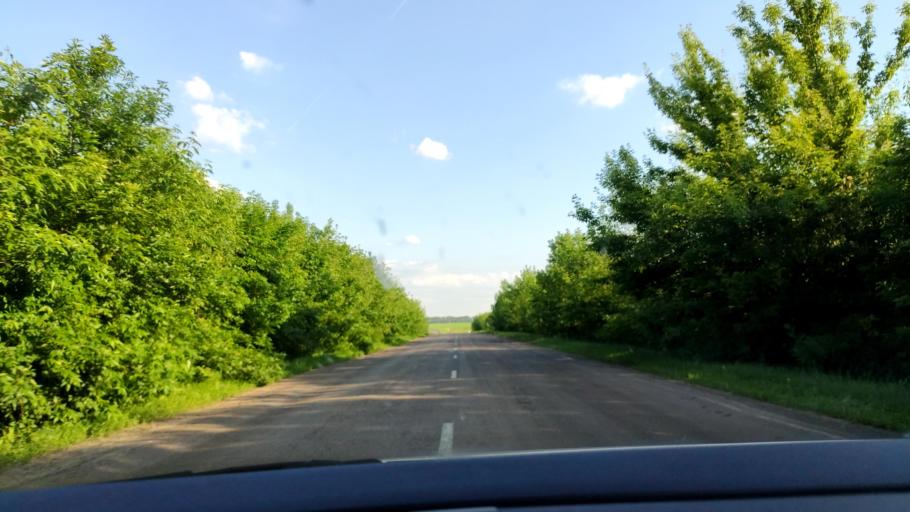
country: RU
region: Voronezj
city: Kashirskoye
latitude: 51.5039
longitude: 39.8323
